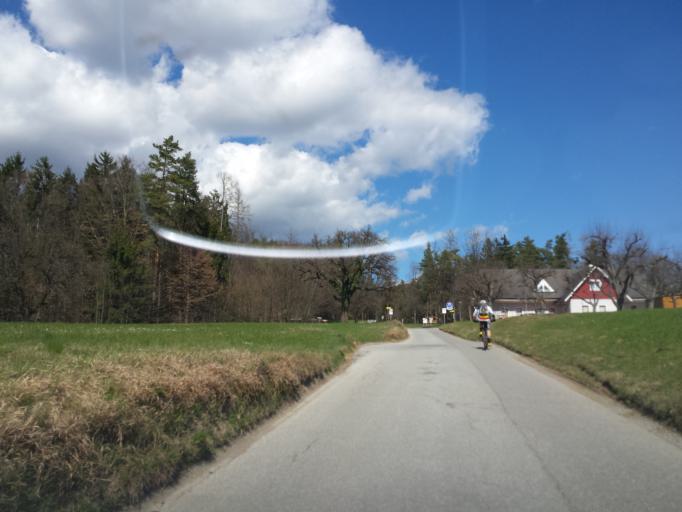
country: AT
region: Styria
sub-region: Politischer Bezirk Graz-Umgebung
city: Stattegg
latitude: 47.1312
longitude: 15.4388
